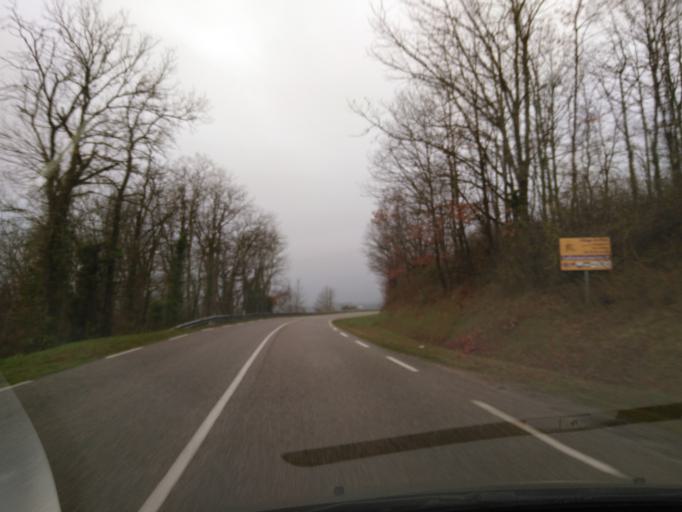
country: FR
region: Aquitaine
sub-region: Departement du Lot-et-Garonne
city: Bias
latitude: 44.4786
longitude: 0.6785
